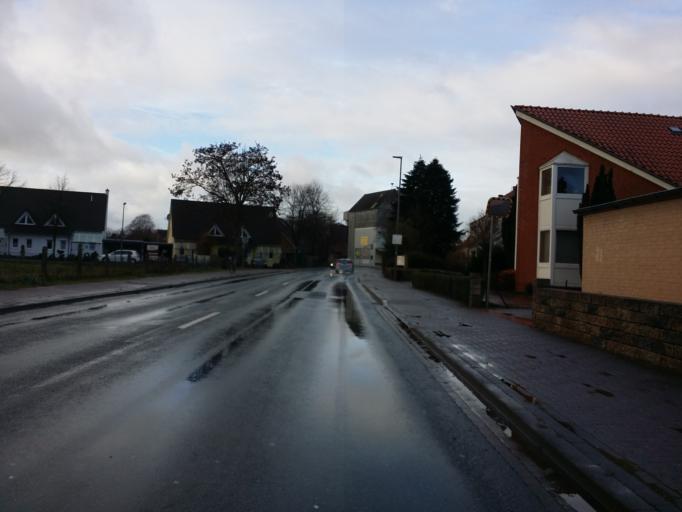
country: DE
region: Lower Saxony
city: Syke
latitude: 52.9862
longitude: 8.8288
